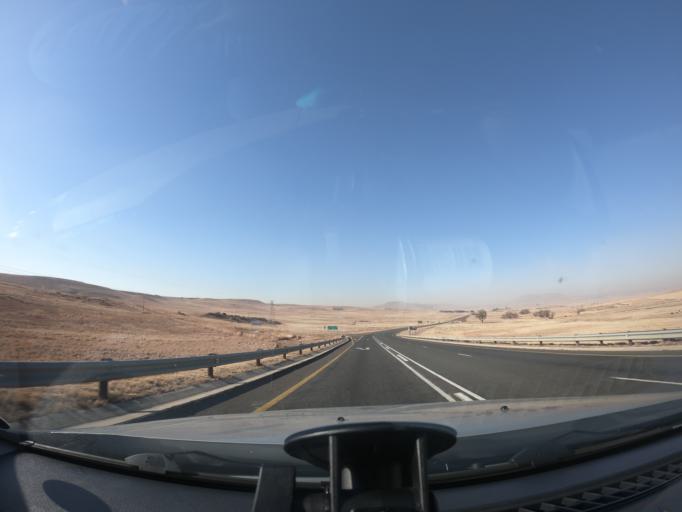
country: ZA
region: Mpumalanga
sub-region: Gert Sibande District Municipality
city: Volksrust
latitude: -27.2155
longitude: 29.8835
